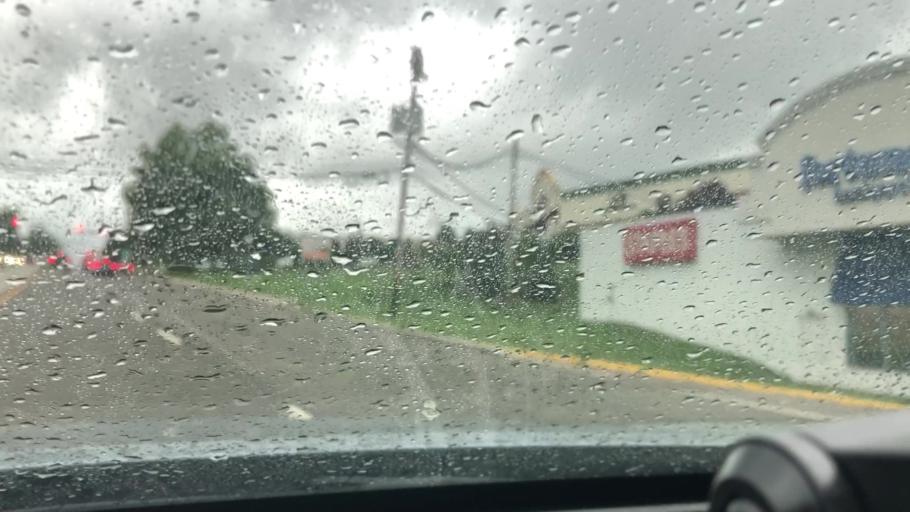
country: US
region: New Jersey
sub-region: Morris County
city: Hanover
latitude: 40.7967
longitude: -74.3472
